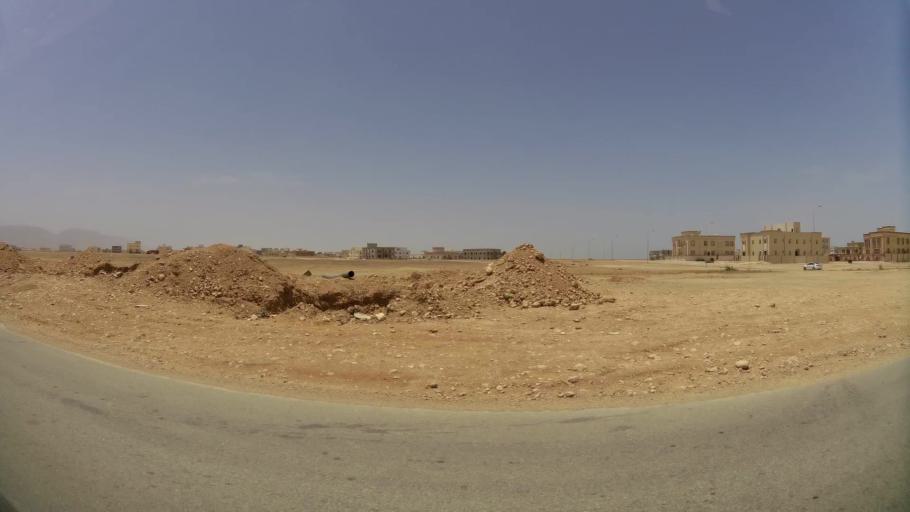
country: OM
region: Zufar
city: Salalah
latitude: 17.0961
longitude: 54.1720
